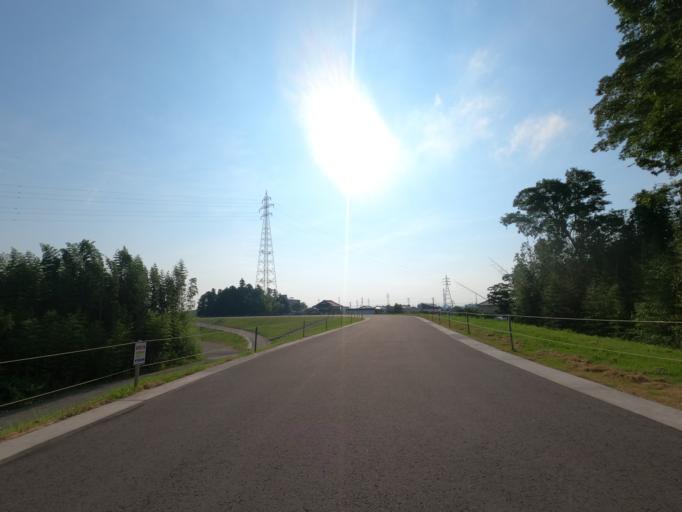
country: JP
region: Ibaraki
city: Mitsukaido
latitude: 36.0106
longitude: 139.9781
